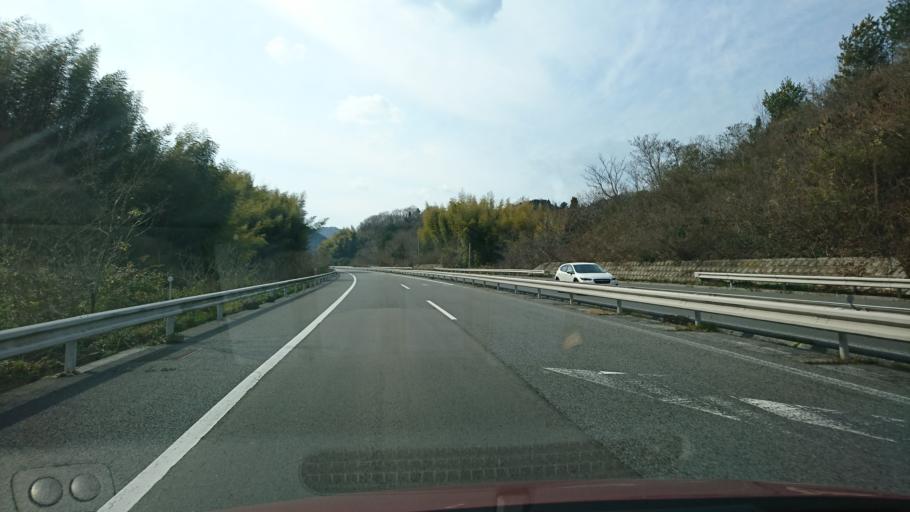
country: JP
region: Hiroshima
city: Innoshima
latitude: 34.1406
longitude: 133.0566
